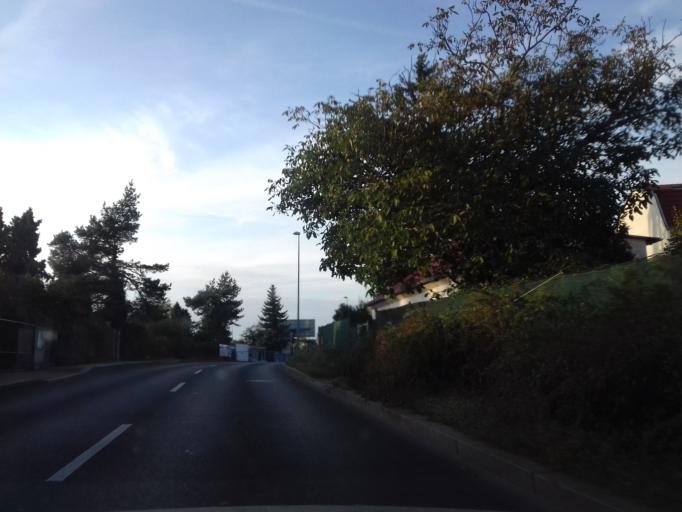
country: CZ
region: Praha
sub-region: Praha 4
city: Hodkovicky
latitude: 50.0152
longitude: 14.4557
